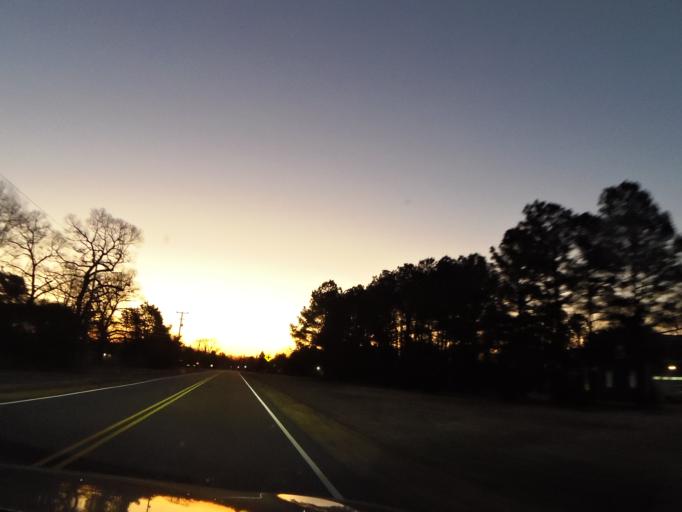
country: US
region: Virginia
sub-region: Henrico County
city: Fort Lee
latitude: 37.4430
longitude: -77.3480
